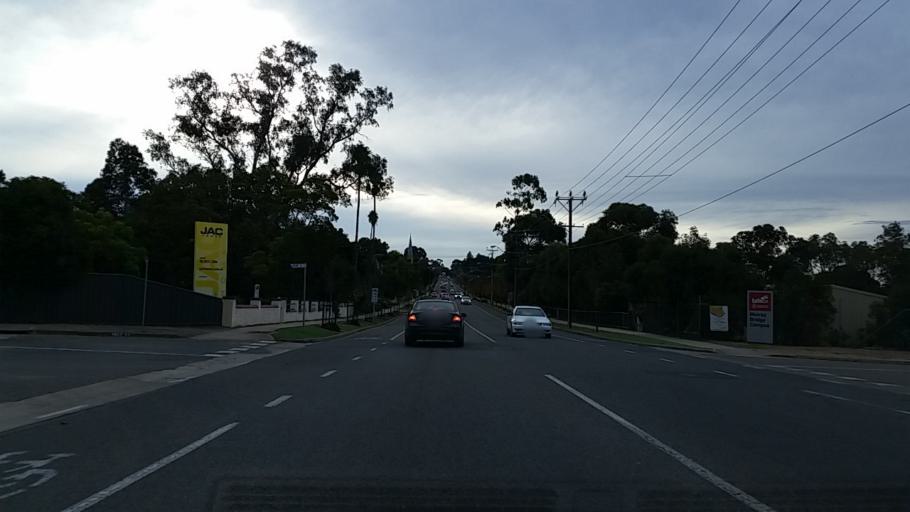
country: AU
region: South Australia
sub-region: Murray Bridge
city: Murray Bridge
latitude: -35.1267
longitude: 139.2781
